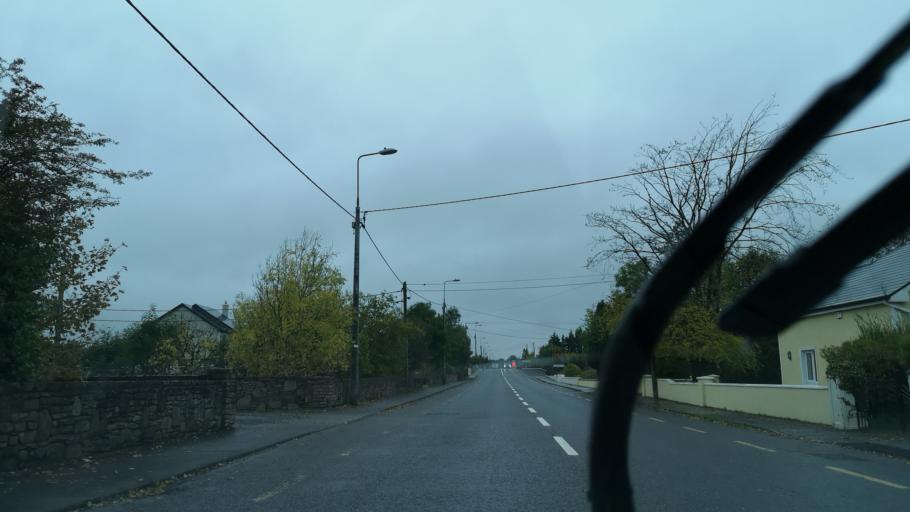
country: IE
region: Connaught
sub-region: Roscommon
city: Ballaghaderreen
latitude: 53.9038
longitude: -8.5841
